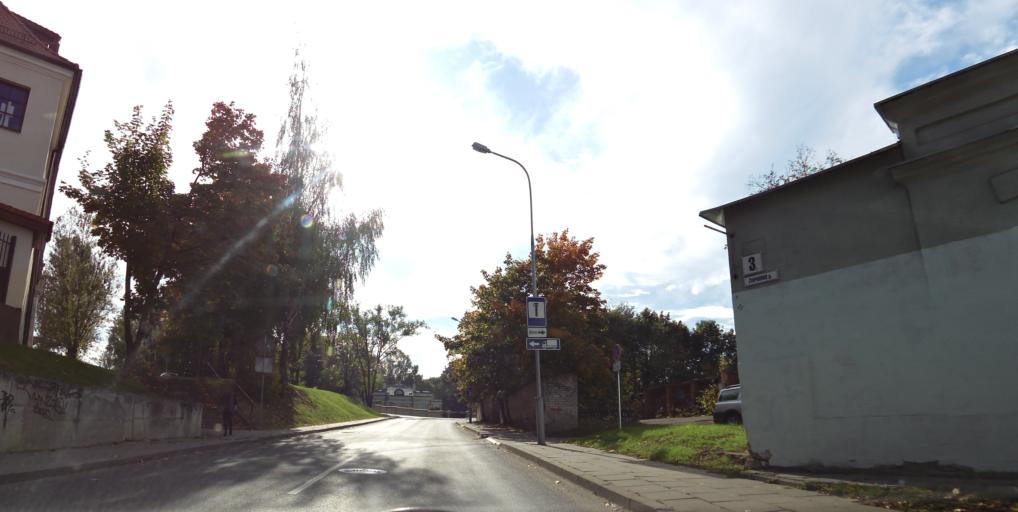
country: LT
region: Vilnius County
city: Rasos
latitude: 54.6762
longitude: 25.2958
